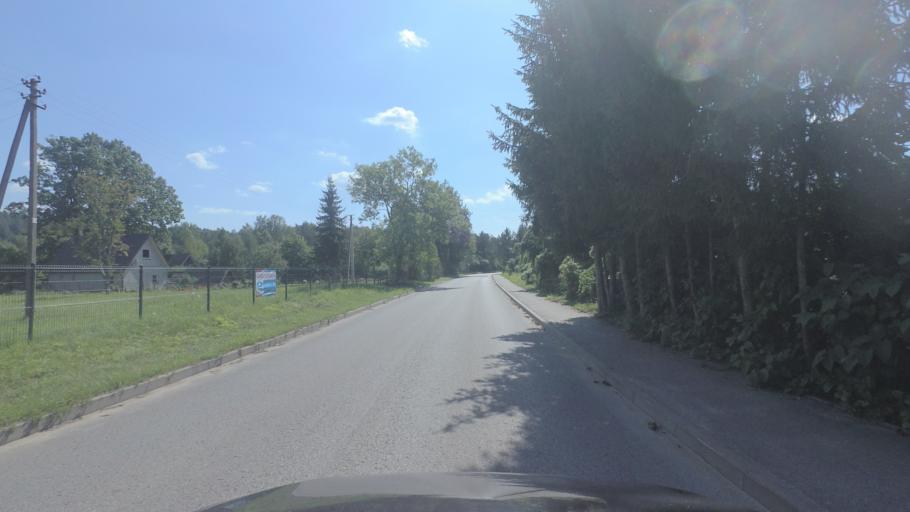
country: LT
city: Nemencine
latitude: 54.8375
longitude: 25.3707
